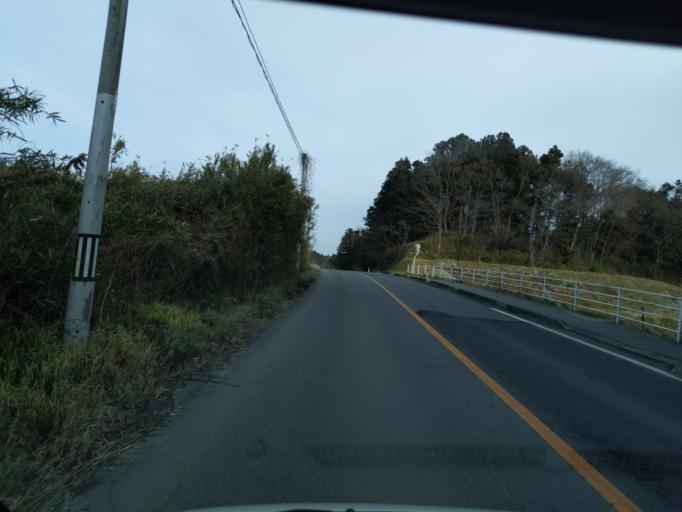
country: JP
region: Miyagi
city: Wakuya
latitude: 38.6921
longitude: 141.1421
